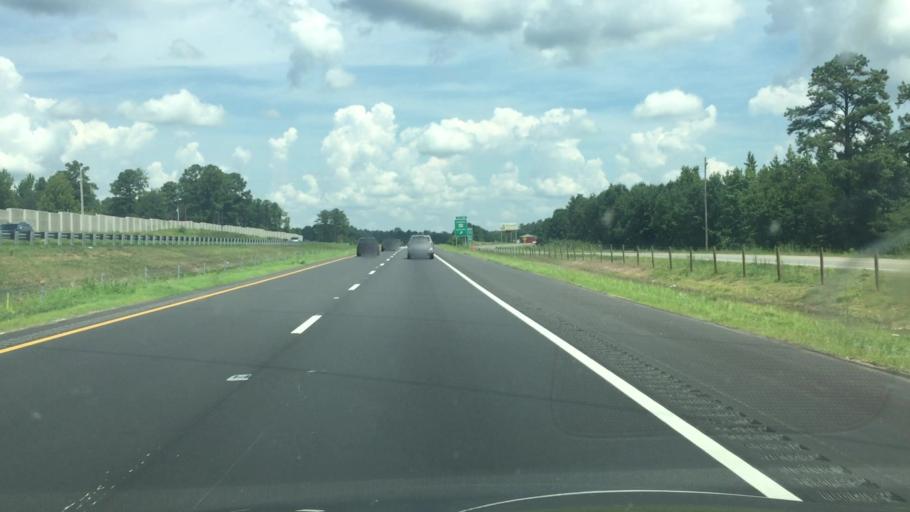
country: US
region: North Carolina
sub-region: Richmond County
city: Ellerbe
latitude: 35.0364
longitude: -79.7687
